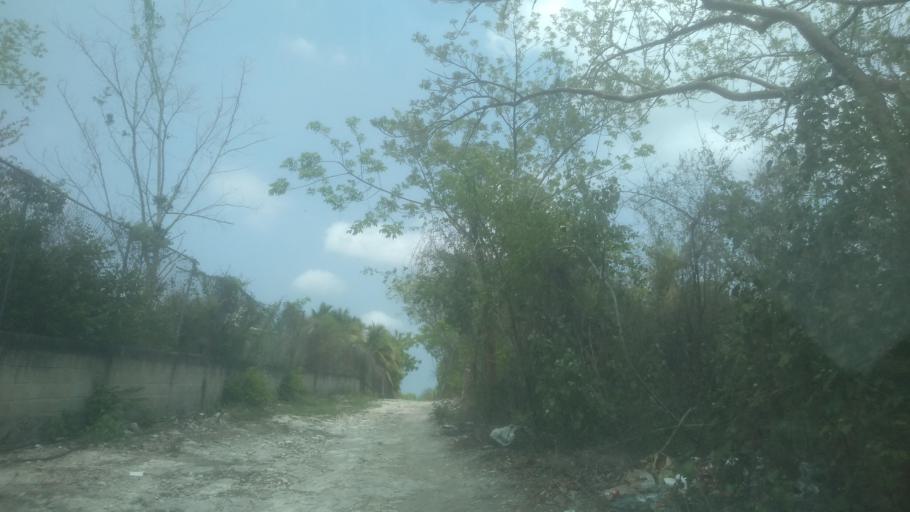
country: MX
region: Veracruz
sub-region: Emiliano Zapata
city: Plan del Rio
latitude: 19.3902
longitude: -96.6328
